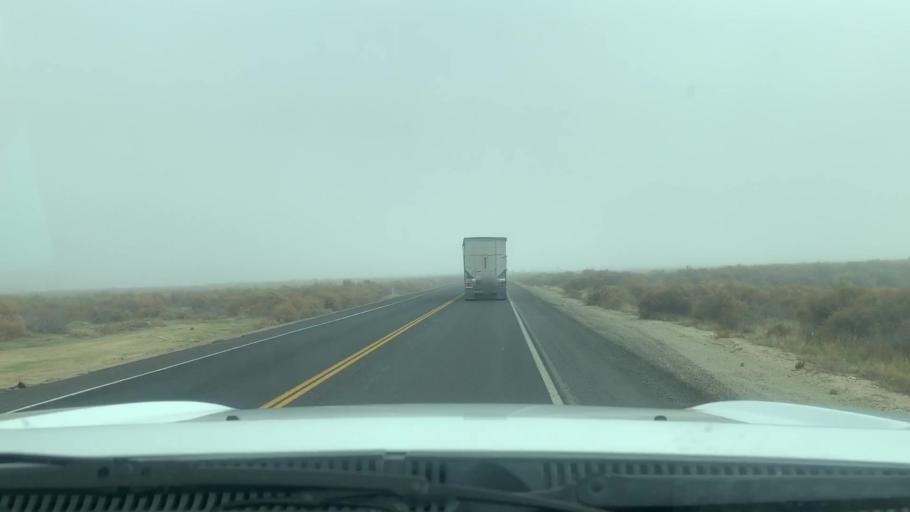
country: US
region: California
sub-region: Kern County
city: Buttonwillow
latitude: 35.4996
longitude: -119.5430
